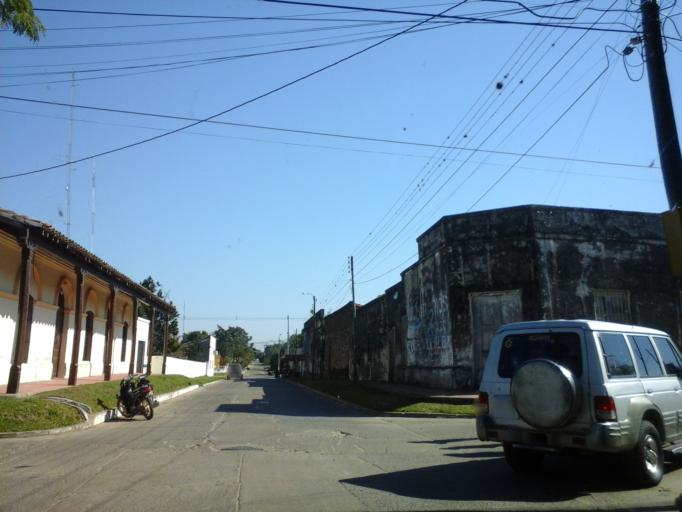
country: PY
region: Neembucu
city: Pilar
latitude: -26.8599
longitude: -58.3054
